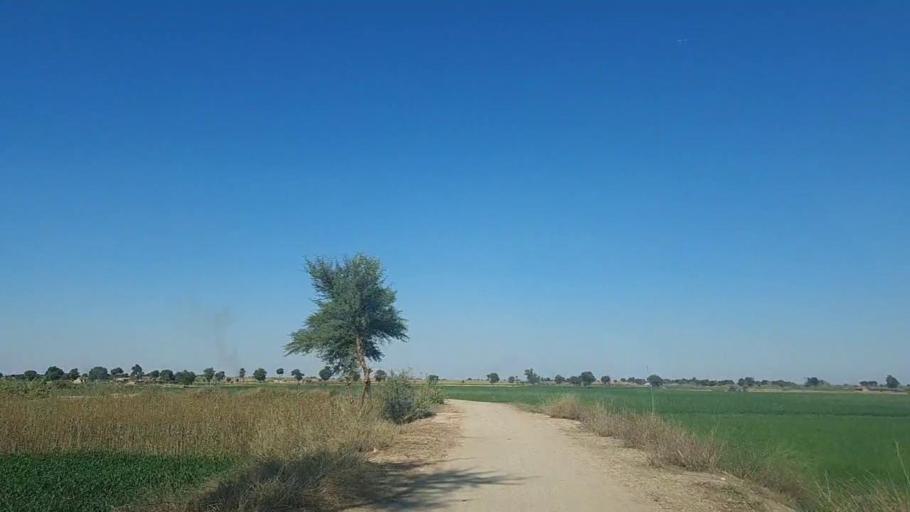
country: PK
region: Sindh
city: Khadro
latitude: 26.2203
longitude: 68.8591
